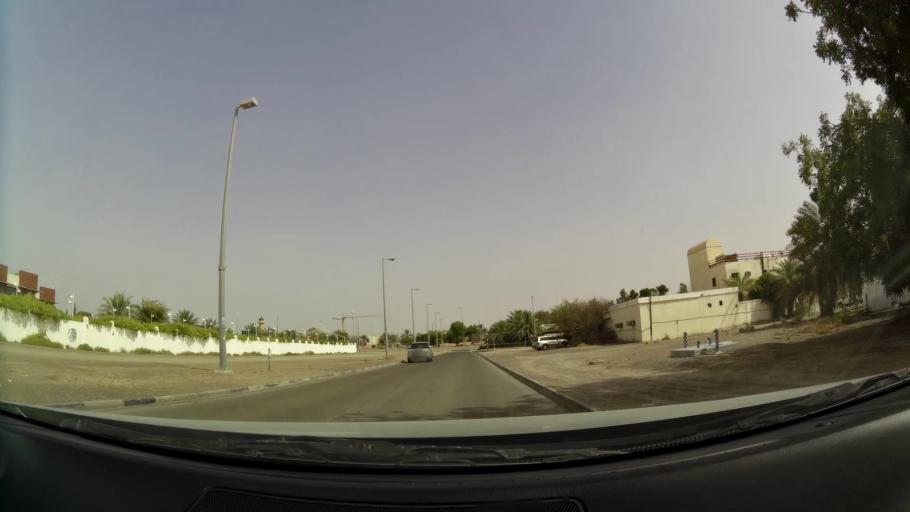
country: AE
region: Abu Dhabi
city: Al Ain
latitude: 24.1916
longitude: 55.6429
